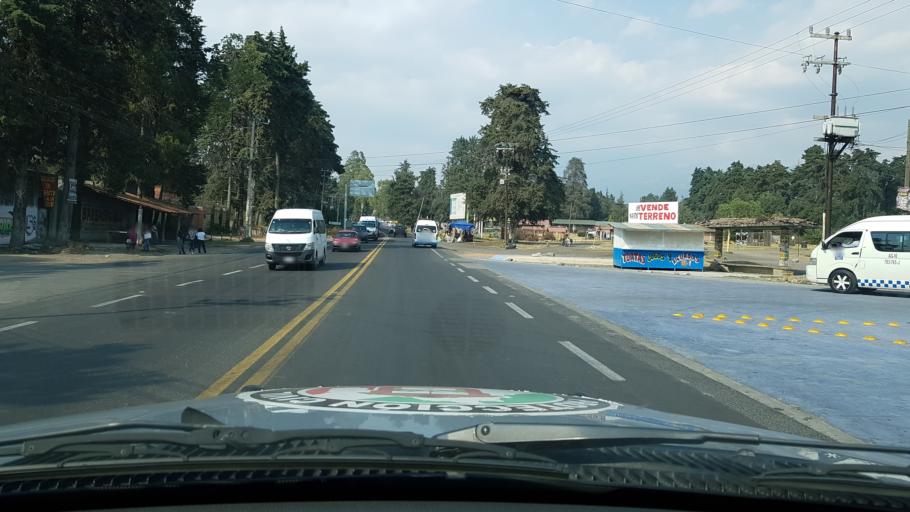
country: MX
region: Mexico
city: Ozumba de Alzate
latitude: 19.0531
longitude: -98.7893
